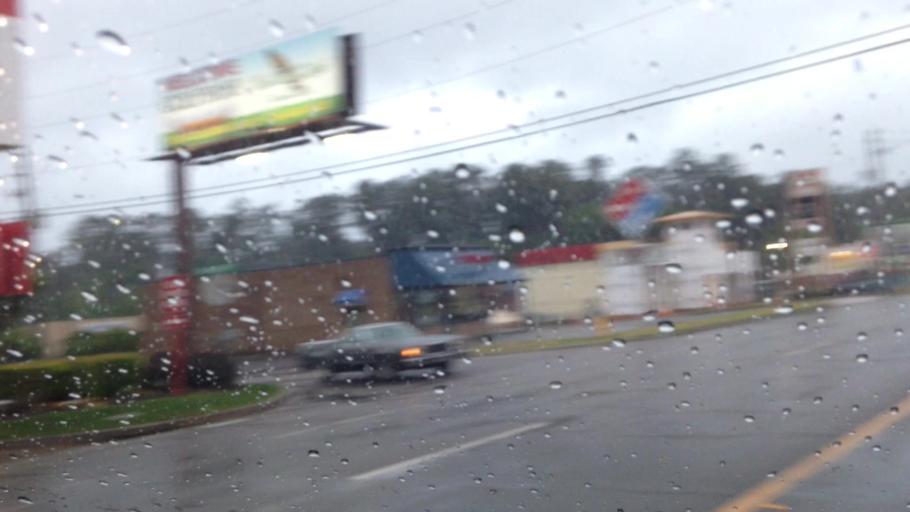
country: US
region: Georgia
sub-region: Columbia County
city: Martinez
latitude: 33.5133
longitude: -82.0519
